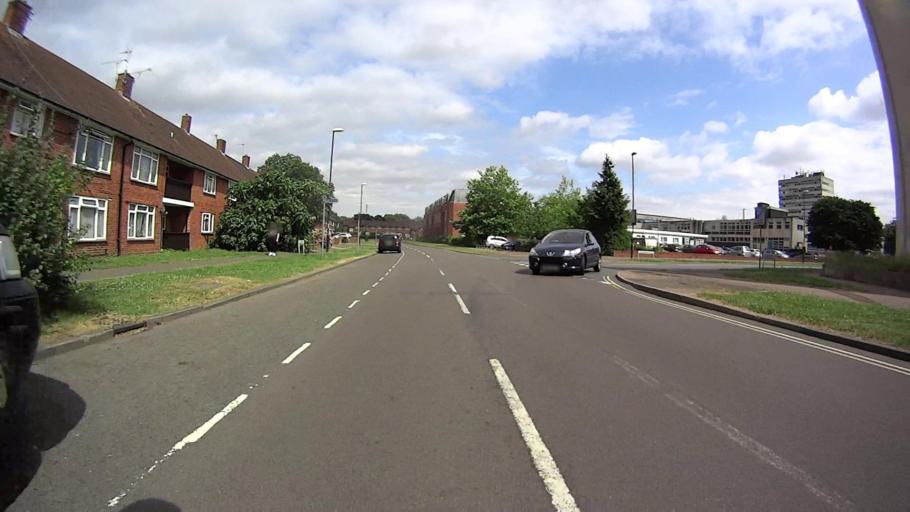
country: GB
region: England
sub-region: West Sussex
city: Crawley
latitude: 51.1183
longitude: -0.1834
